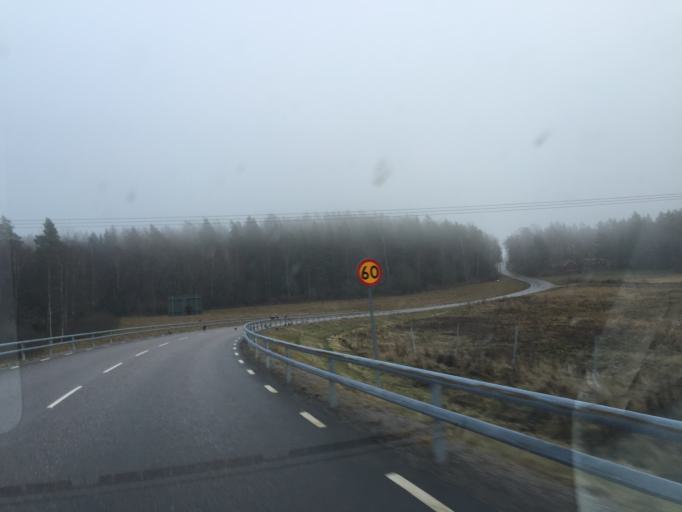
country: SE
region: Stockholm
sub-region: Nynashamns Kommun
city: Osmo
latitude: 59.0259
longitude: 17.9527
